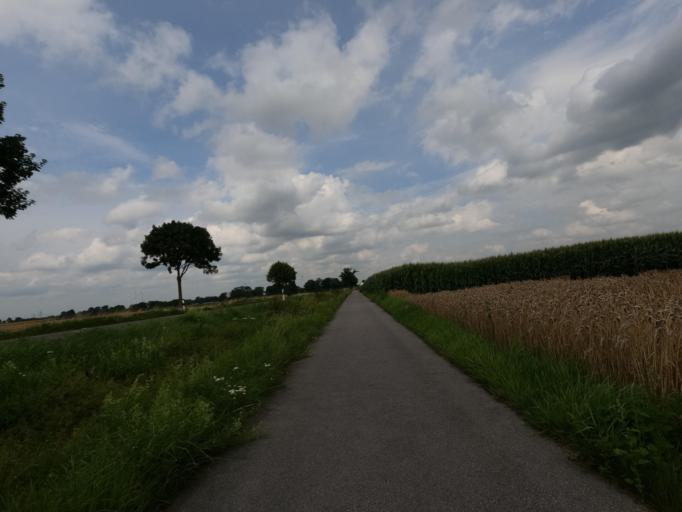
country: DE
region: North Rhine-Westphalia
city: Baesweiler
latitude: 50.9501
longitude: 6.2192
